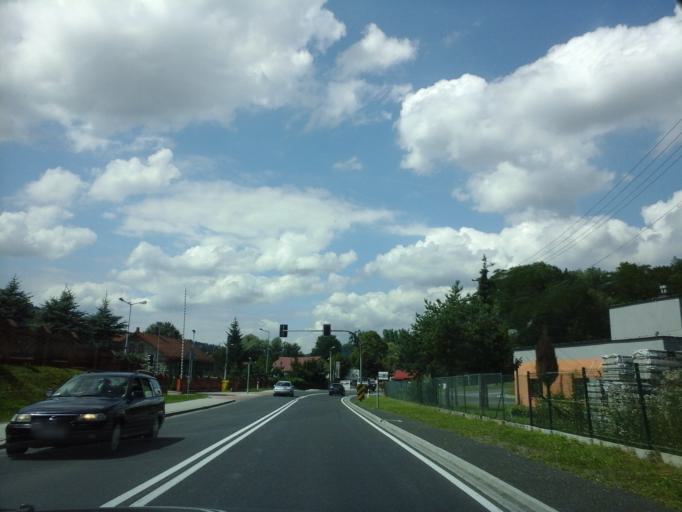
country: PL
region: Lesser Poland Voivodeship
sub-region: Powiat suski
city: Sucha Beskidzka
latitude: 49.7355
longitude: 19.6199
